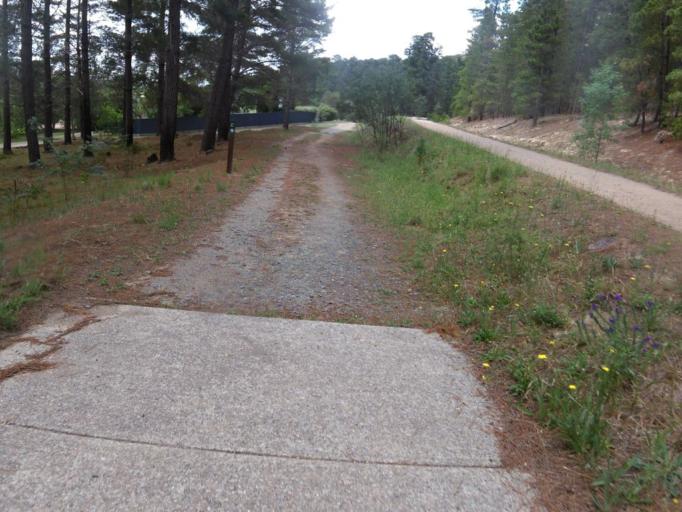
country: AU
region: Australian Capital Territory
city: Macarthur
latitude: -35.3765
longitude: 149.1187
